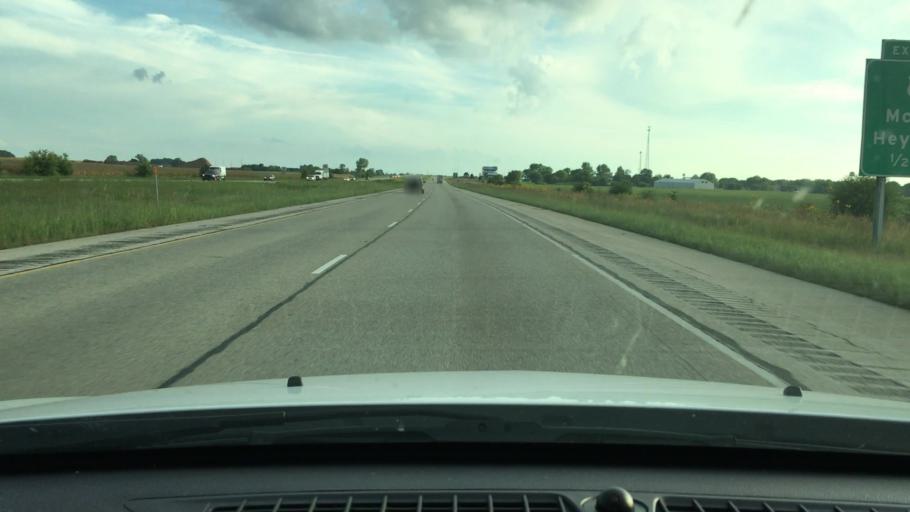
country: US
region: Illinois
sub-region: Logan County
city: Atlanta
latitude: 40.3235
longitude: -89.1564
